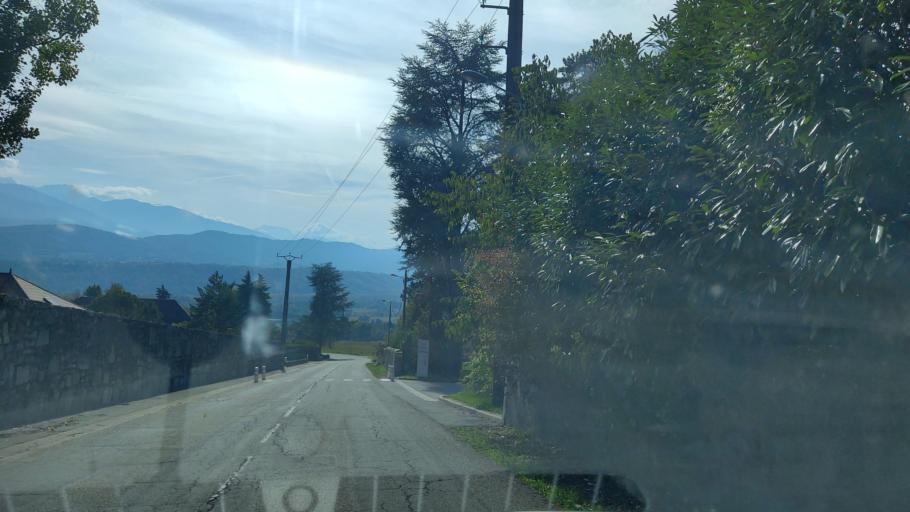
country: FR
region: Rhone-Alpes
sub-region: Departement de la Savoie
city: Coise-Saint-Jean-Pied-Gauthier
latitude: 45.5695
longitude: 6.1518
